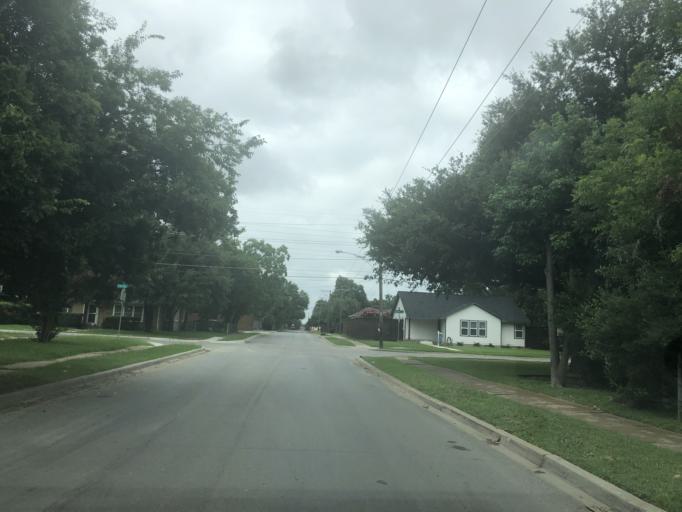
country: US
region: Texas
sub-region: Dallas County
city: University Park
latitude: 32.8667
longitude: -96.8530
